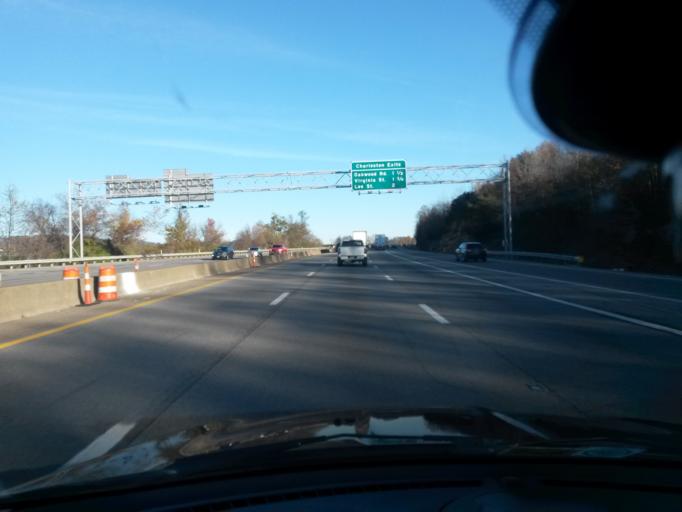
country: US
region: West Virginia
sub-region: Kanawha County
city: South Charleston
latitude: 38.3649
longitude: -81.6828
